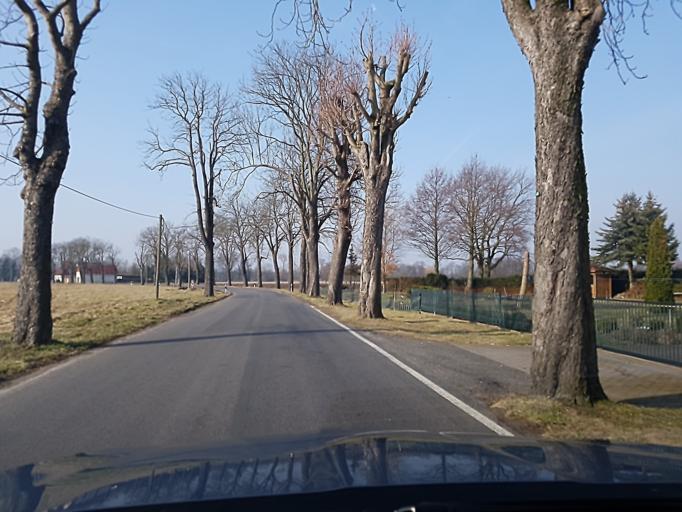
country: DE
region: Brandenburg
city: Falkenberg
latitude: 51.6391
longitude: 13.2896
